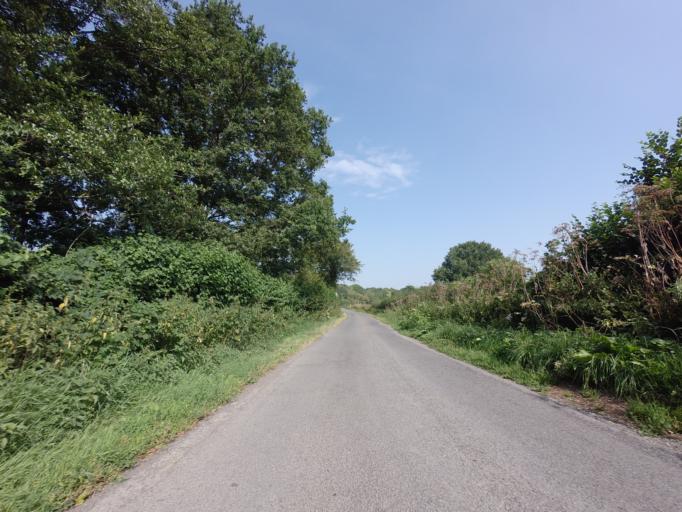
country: GB
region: England
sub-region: Kent
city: Staplehurst
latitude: 51.1222
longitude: 0.5895
